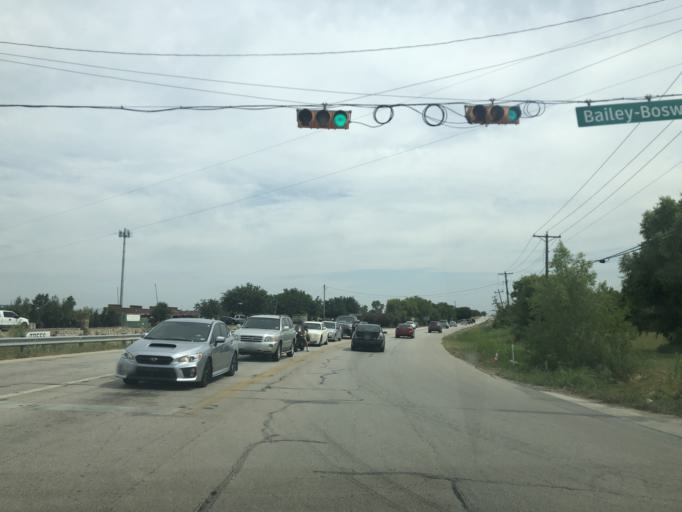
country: US
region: Texas
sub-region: Tarrant County
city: Blue Mound
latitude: 32.8837
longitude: -97.3427
